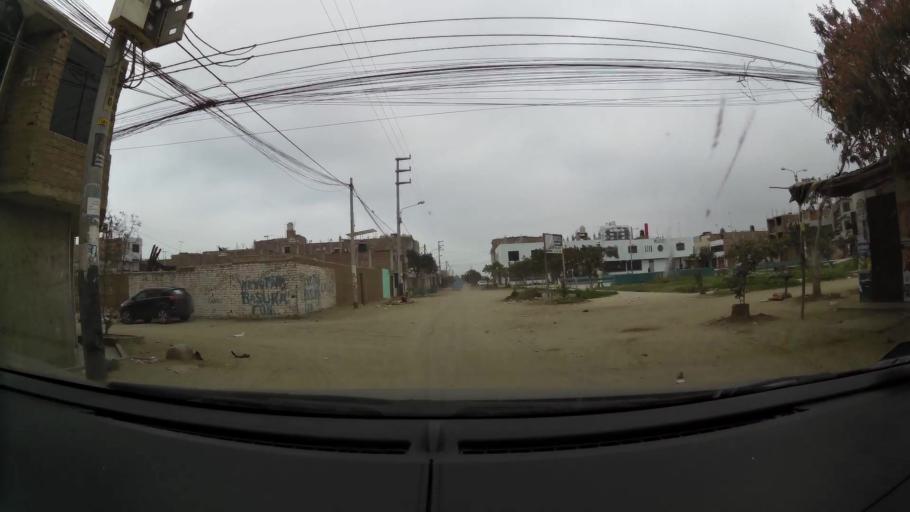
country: PE
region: La Libertad
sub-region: Provincia de Trujillo
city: La Esperanza
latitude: -8.0890
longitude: -79.0442
